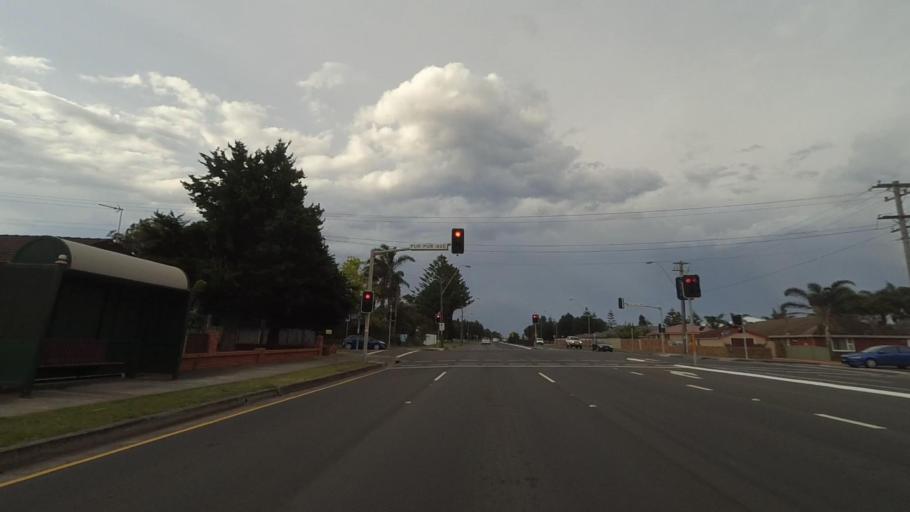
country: AU
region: New South Wales
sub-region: Shellharbour
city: Lake Illawarra
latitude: -34.5412
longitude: 150.8642
